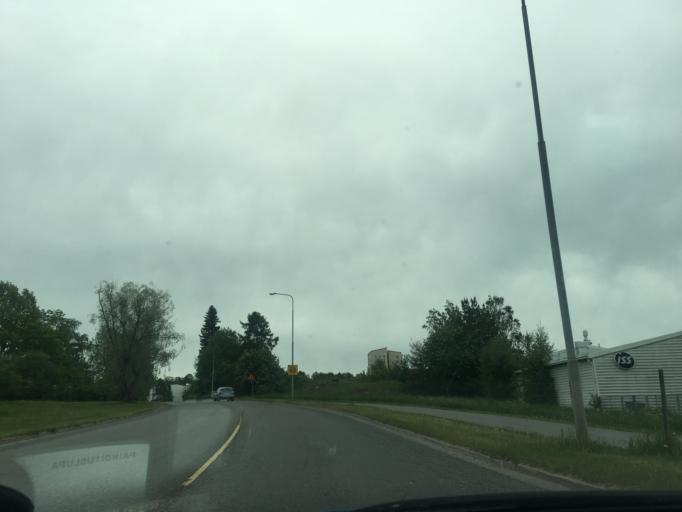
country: FI
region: Varsinais-Suomi
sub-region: Turku
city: Turku
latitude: 60.4637
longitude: 22.3037
